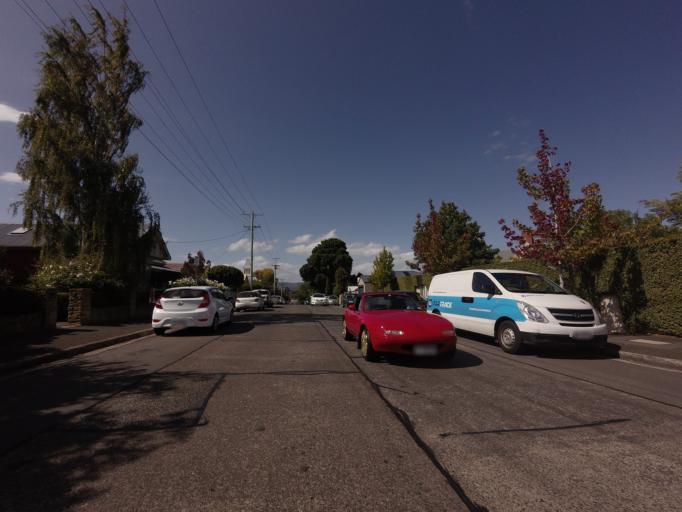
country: AU
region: Tasmania
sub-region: Hobart
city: Sandy Bay
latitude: -42.8970
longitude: 147.3192
